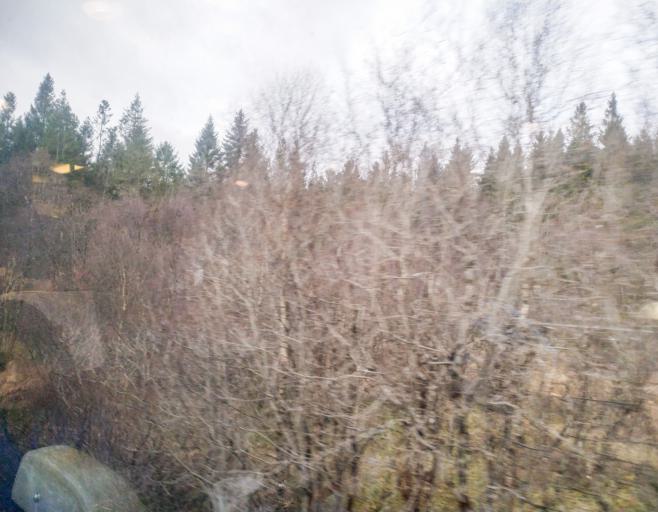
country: GB
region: Scotland
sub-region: Highland
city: Spean Bridge
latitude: 56.8922
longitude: -4.9047
